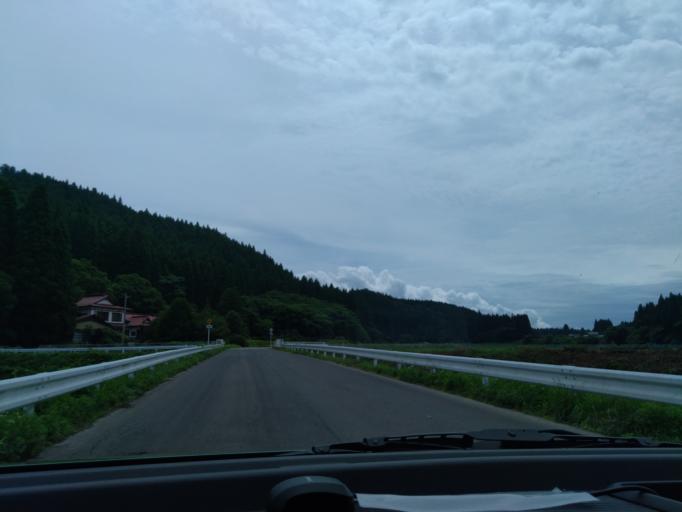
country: JP
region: Akita
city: Kakunodatemachi
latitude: 39.5945
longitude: 140.6182
